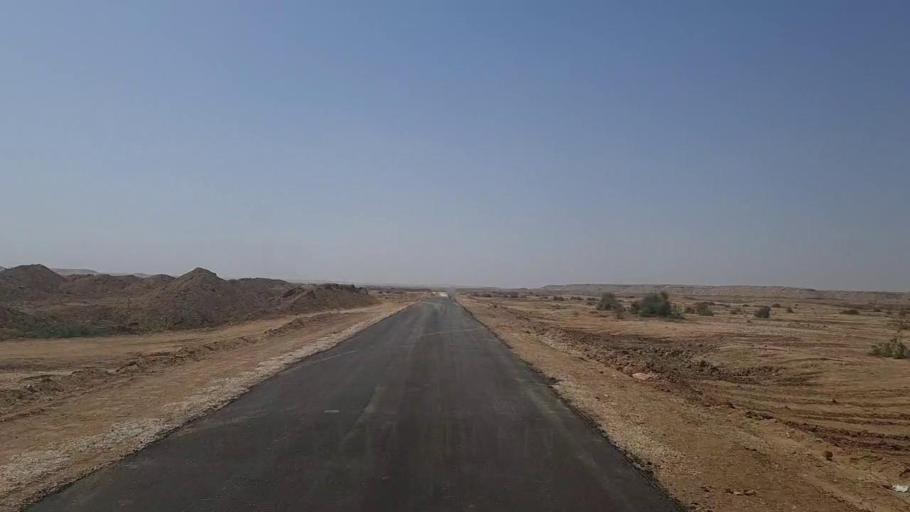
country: PK
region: Sindh
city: Kotri
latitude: 25.1465
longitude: 68.1972
